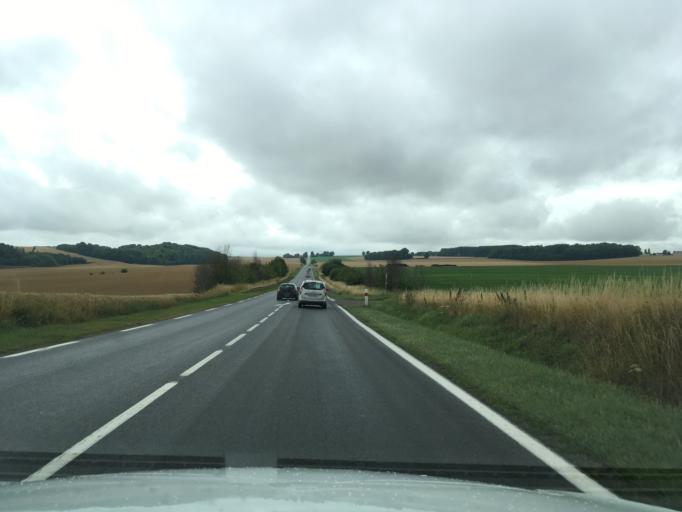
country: FR
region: Picardie
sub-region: Departement de l'Aisne
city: Ribemont
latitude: 49.8425
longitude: 3.4240
